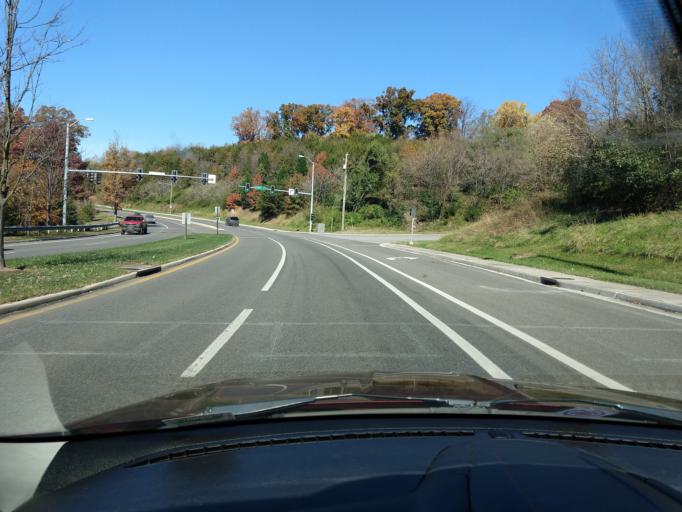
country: US
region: Virginia
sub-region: Roanoke County
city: Cave Spring
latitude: 37.2735
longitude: -80.0073
